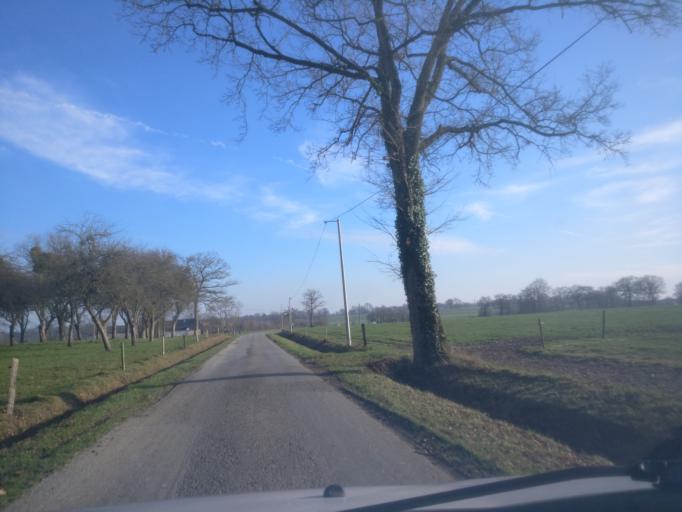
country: FR
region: Brittany
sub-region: Departement d'Ille-et-Vilaine
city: Livre-sur-Changeon
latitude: 48.2162
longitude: -1.3109
